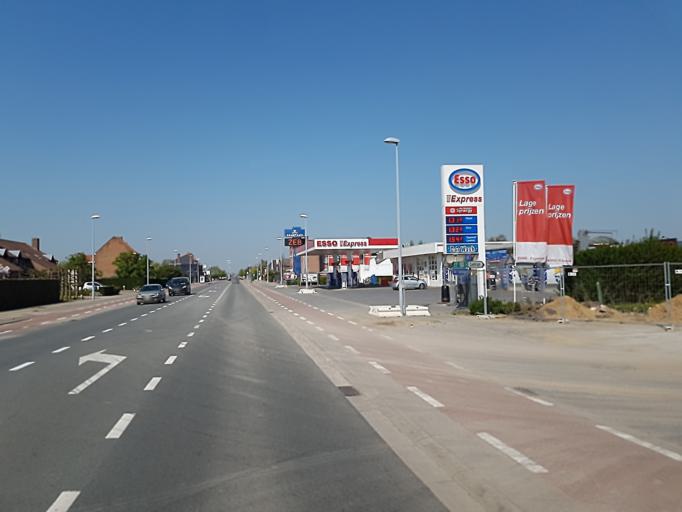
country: BE
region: Flanders
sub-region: Provincie West-Vlaanderen
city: Menen
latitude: 50.8020
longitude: 3.1031
